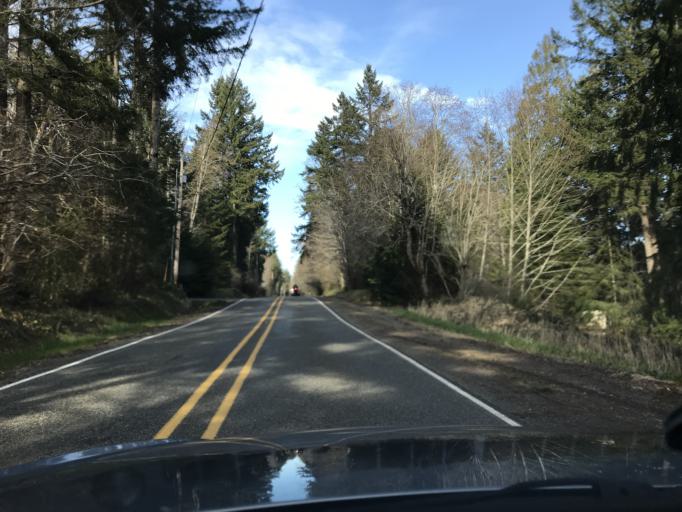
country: US
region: Washington
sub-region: Pierce County
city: Longbranch
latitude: 47.2365
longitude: -122.7883
